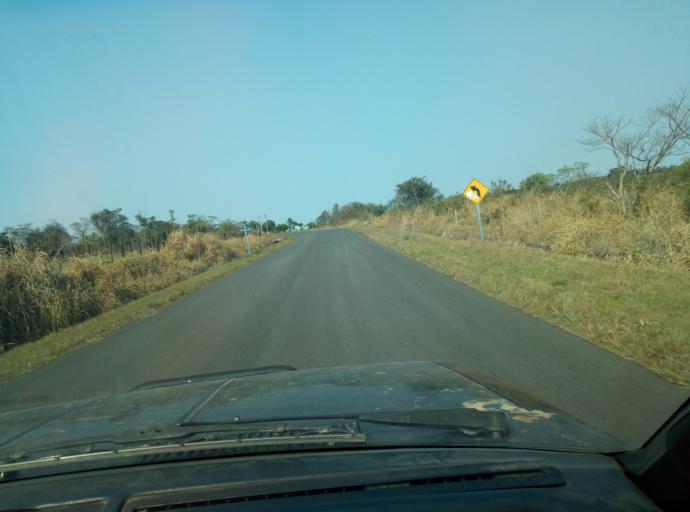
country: PY
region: Caaguazu
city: Carayao
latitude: -25.1852
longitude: -56.3124
